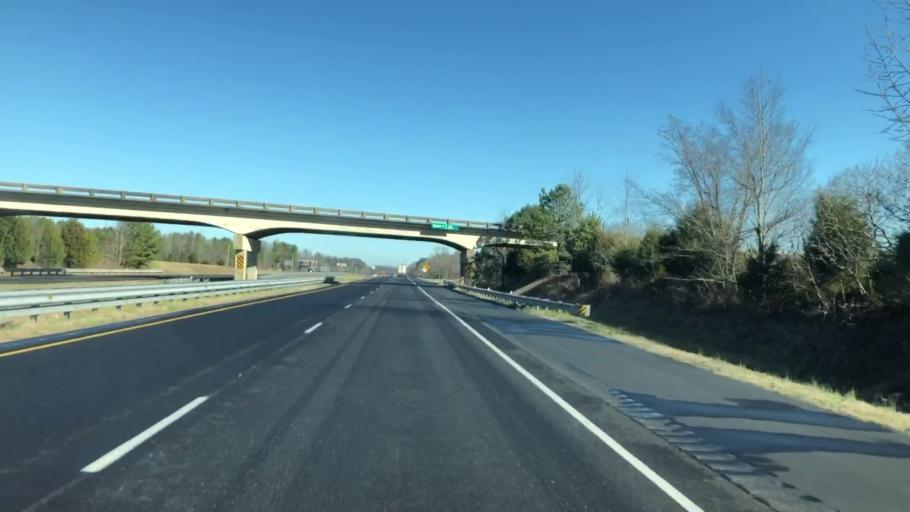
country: US
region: Alabama
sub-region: Limestone County
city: Ardmore
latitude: 34.9194
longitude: -86.9065
